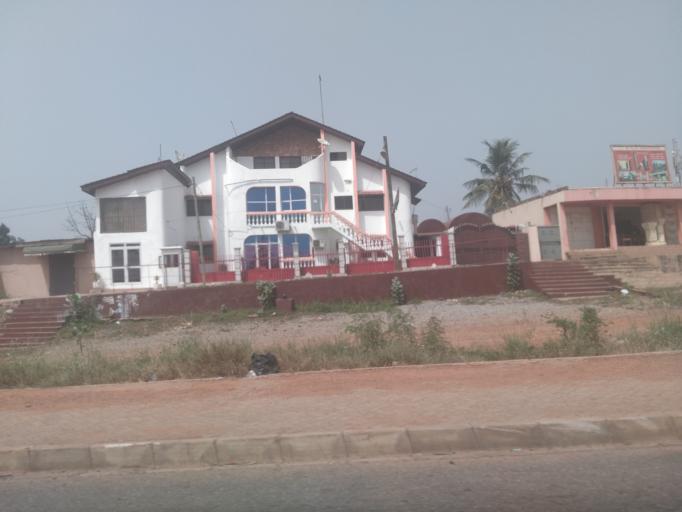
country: GH
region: Greater Accra
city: Dome
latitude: 5.6143
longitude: -0.2212
